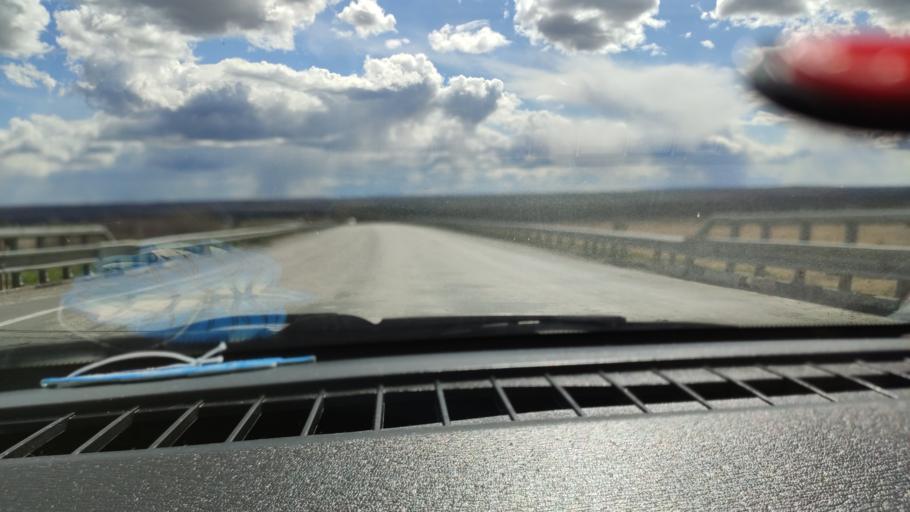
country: RU
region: Samara
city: Varlamovo
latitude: 53.1685
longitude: 48.2809
